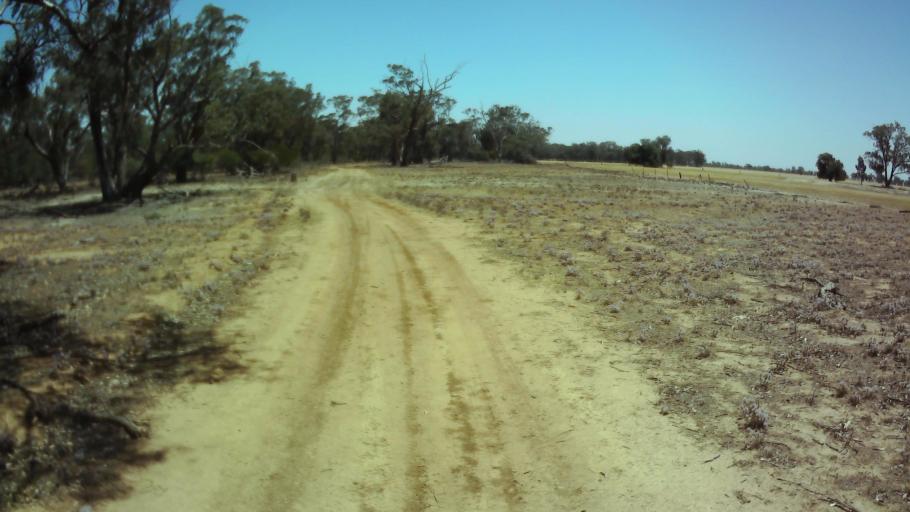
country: AU
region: New South Wales
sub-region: Weddin
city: Grenfell
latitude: -34.0668
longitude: 147.7986
